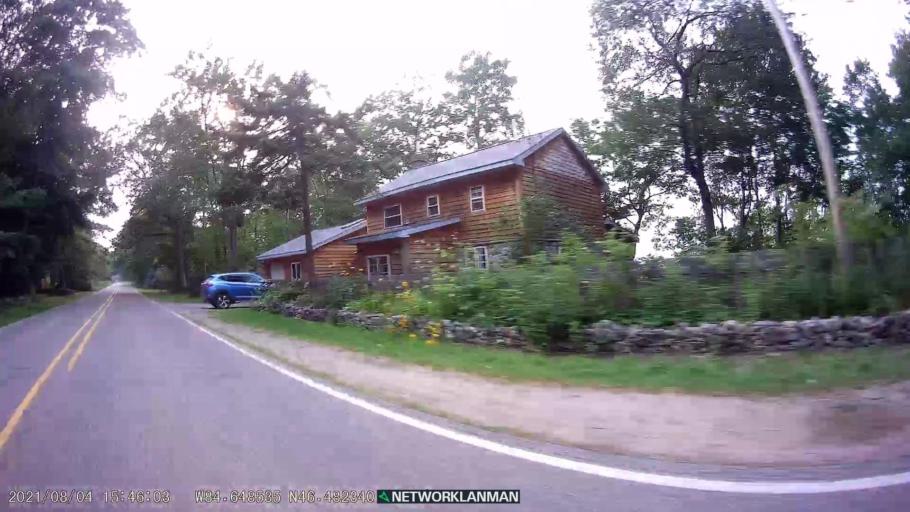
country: US
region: Michigan
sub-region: Chippewa County
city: Sault Ste. Marie
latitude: 46.4825
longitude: -84.6488
